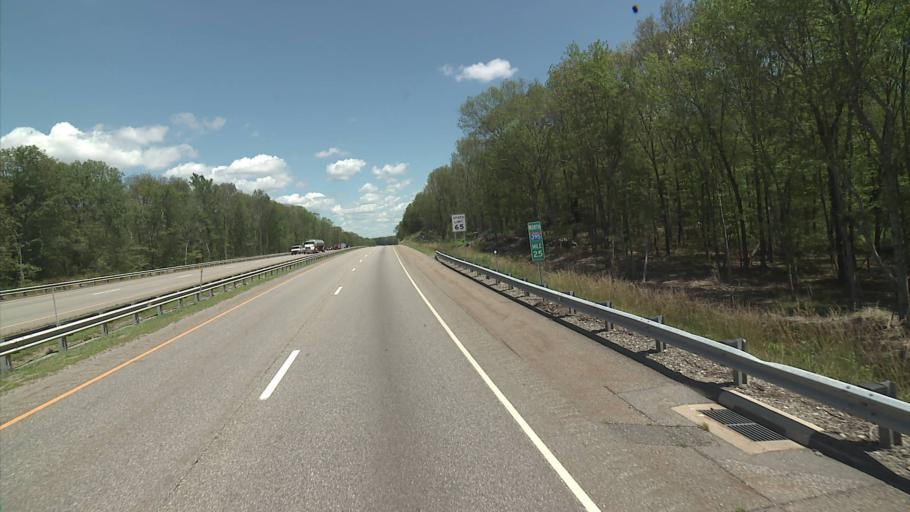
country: US
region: Connecticut
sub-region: New London County
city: Jewett City
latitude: 41.6226
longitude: -71.9435
